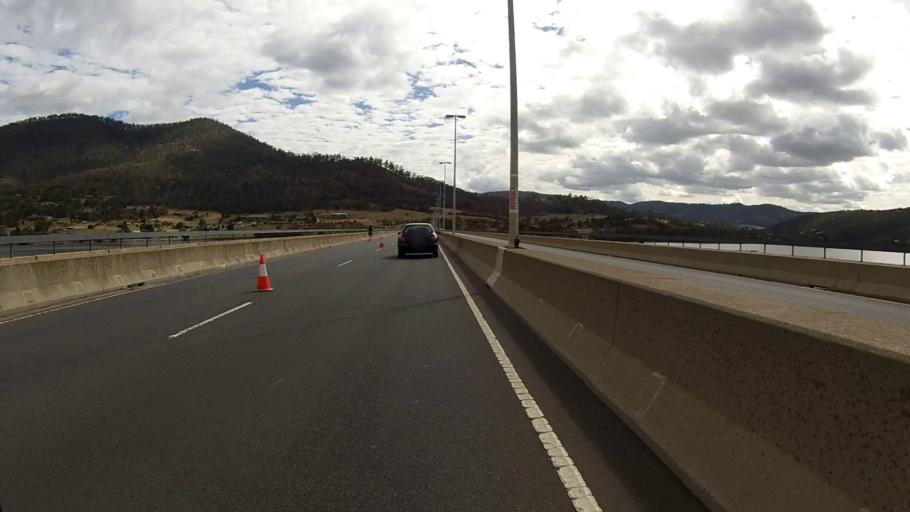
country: AU
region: Tasmania
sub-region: Glenorchy
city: Goodwood
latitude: -42.8190
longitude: 147.3055
